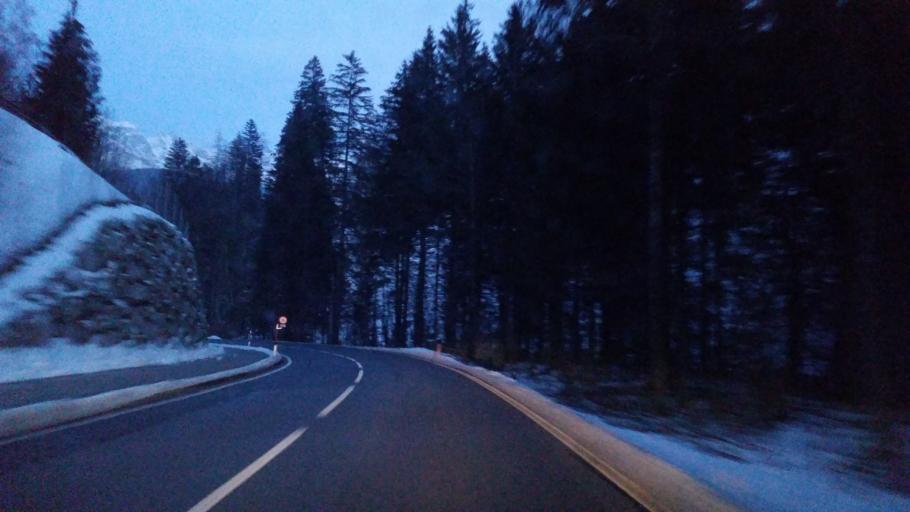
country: AT
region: Salzburg
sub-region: Politischer Bezirk Hallein
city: Abtenau
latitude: 47.5027
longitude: 13.4222
